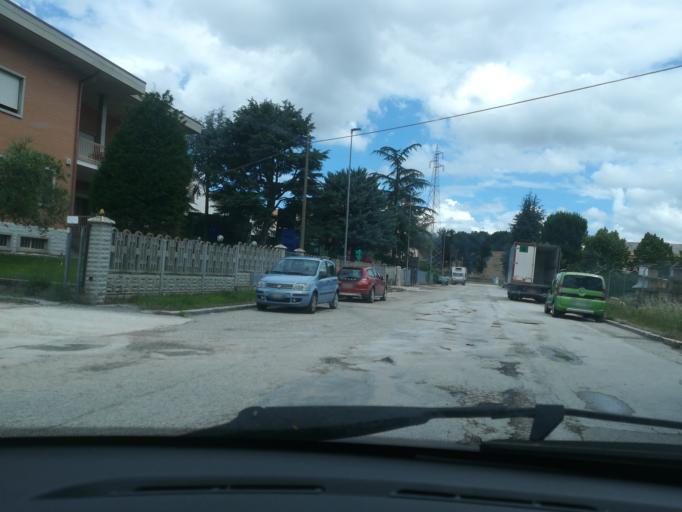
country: IT
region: The Marches
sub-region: Provincia di Macerata
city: Sforzacosta
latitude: 43.2580
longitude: 13.4272
